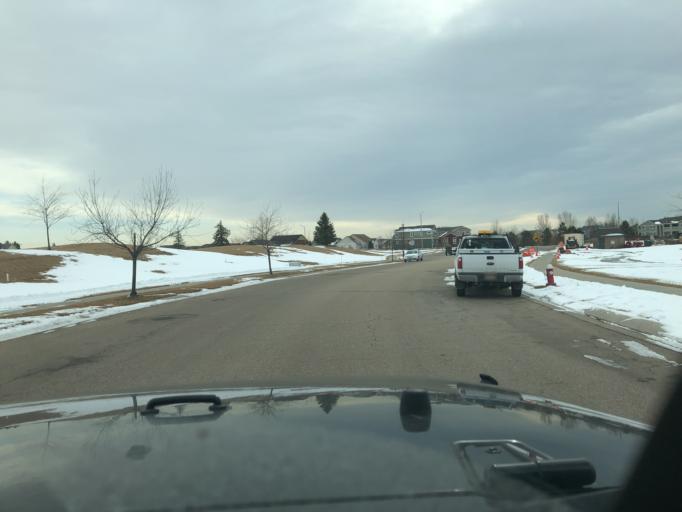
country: US
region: Colorado
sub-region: Boulder County
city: Longmont
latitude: 40.1904
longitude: -105.0639
